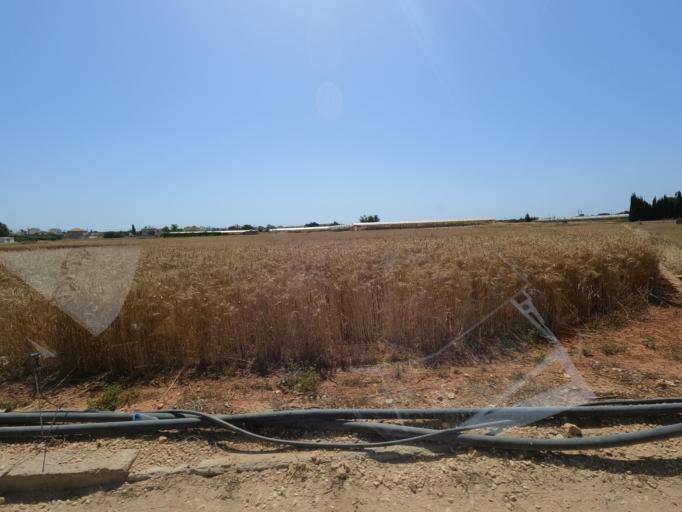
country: CY
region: Ammochostos
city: Frenaros
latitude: 35.0158
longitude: 33.9504
